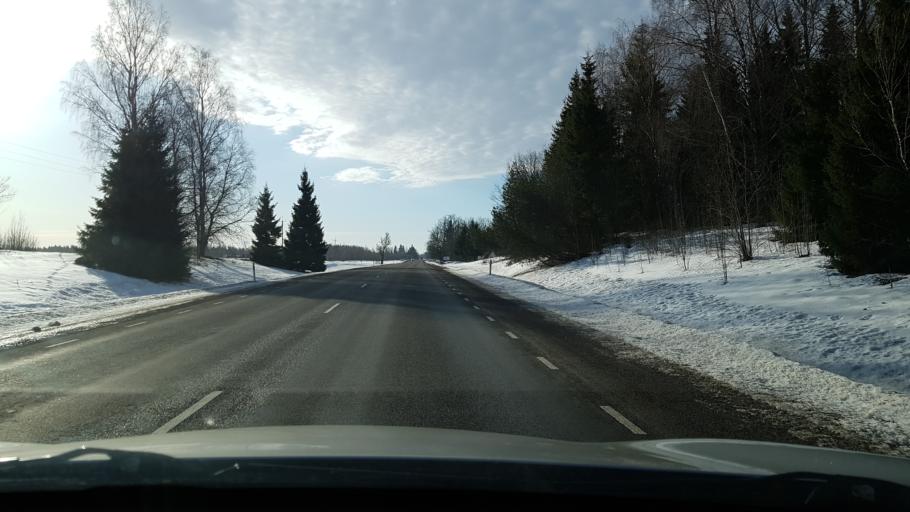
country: EE
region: Viljandimaa
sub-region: Viljandi linn
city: Viljandi
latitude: 58.4469
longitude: 25.5957
